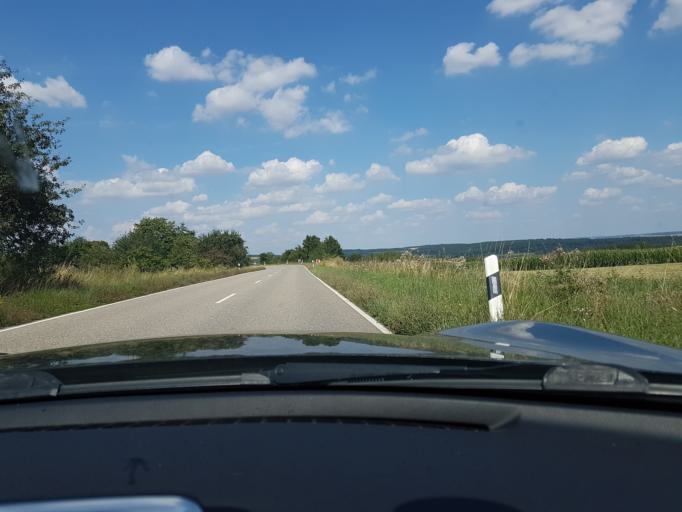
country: DE
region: Baden-Wuerttemberg
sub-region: Regierungsbezirk Stuttgart
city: Offenau
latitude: 49.2631
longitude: 9.1393
